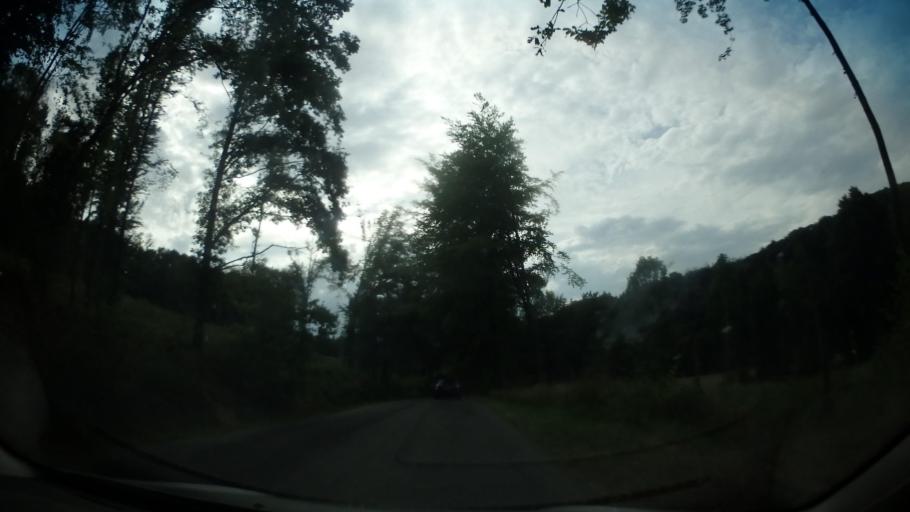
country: CZ
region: Pardubicky
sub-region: Okres Chrudim
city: Sec
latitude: 49.8422
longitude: 15.6834
